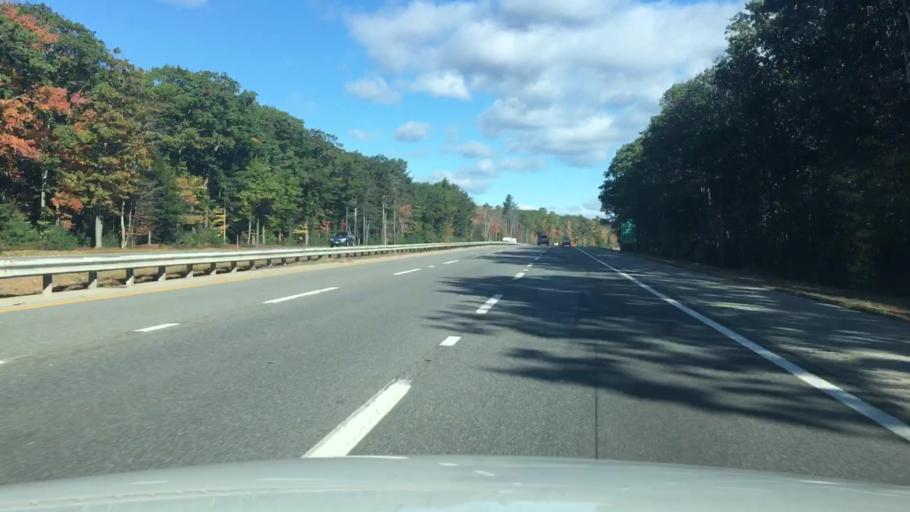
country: US
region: Maine
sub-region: York County
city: Wells Beach Station
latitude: 43.3081
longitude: -70.6147
